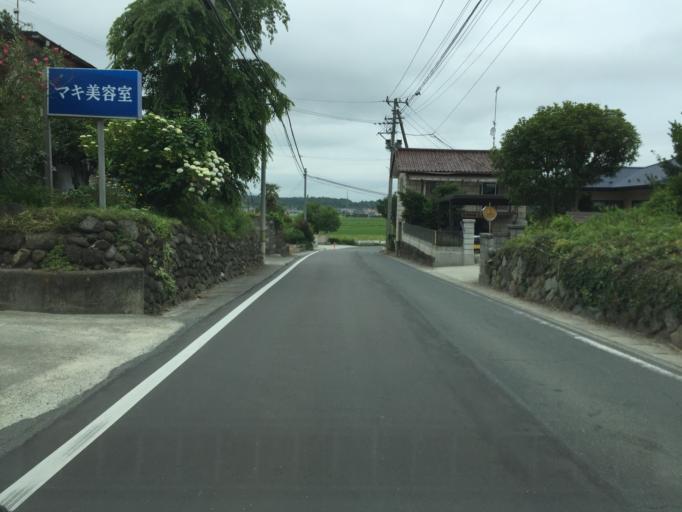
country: JP
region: Miyagi
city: Marumori
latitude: 37.7770
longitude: 140.9117
